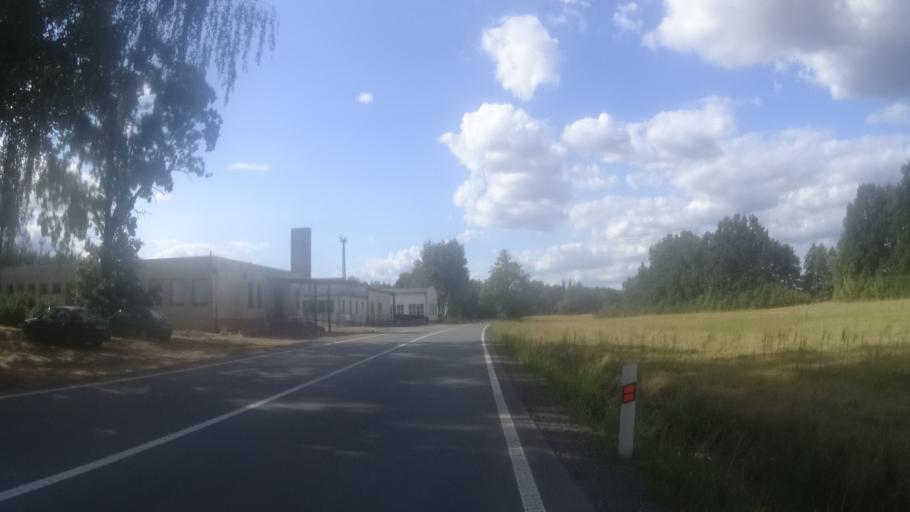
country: CZ
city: Borohradek
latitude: 50.1046
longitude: 16.0819
